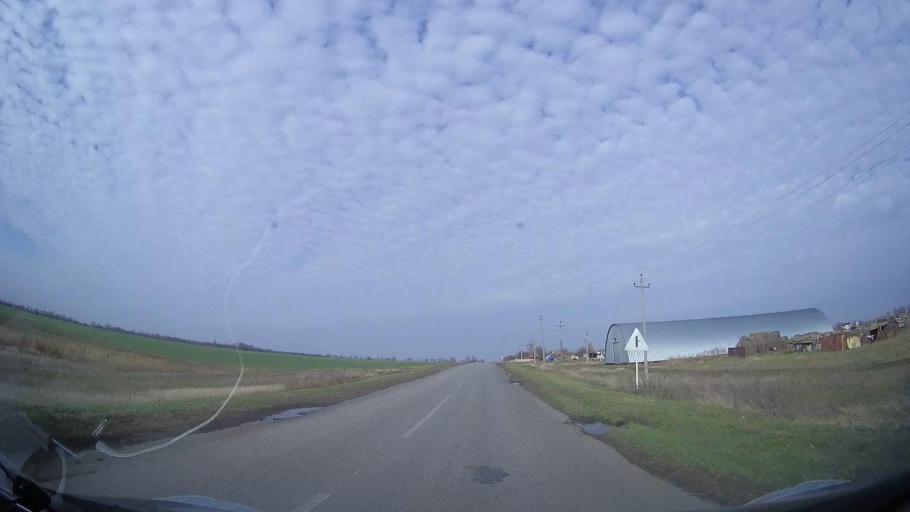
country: RU
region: Rostov
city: Gigant
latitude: 46.9217
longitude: 41.2487
